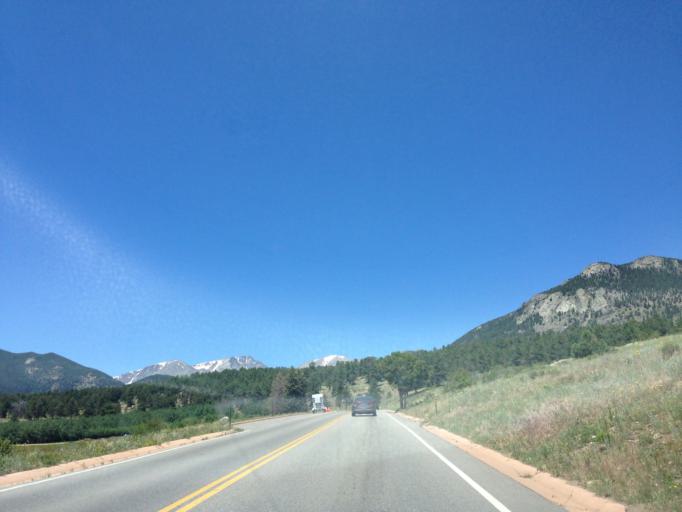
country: US
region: Colorado
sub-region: Larimer County
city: Estes Park
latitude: 40.3570
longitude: -105.5843
